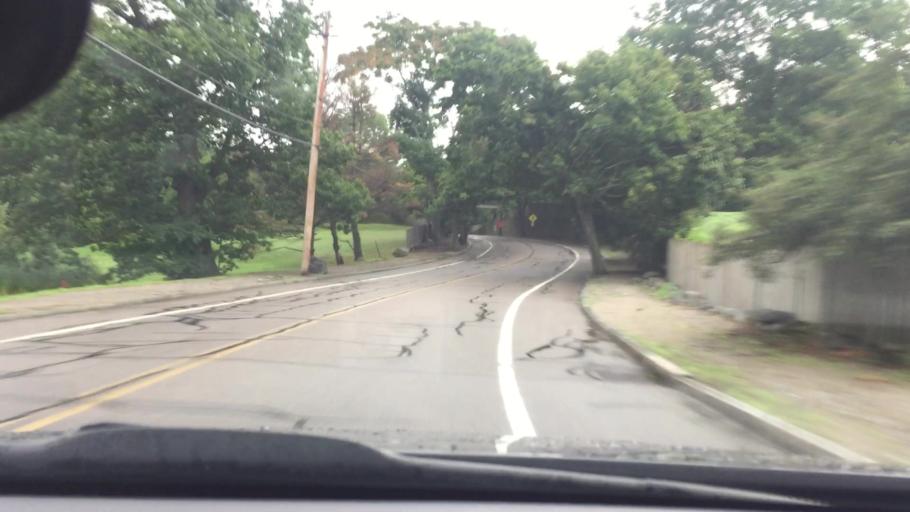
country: US
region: Massachusetts
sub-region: Middlesex County
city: Newton
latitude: 42.3000
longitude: -71.1920
